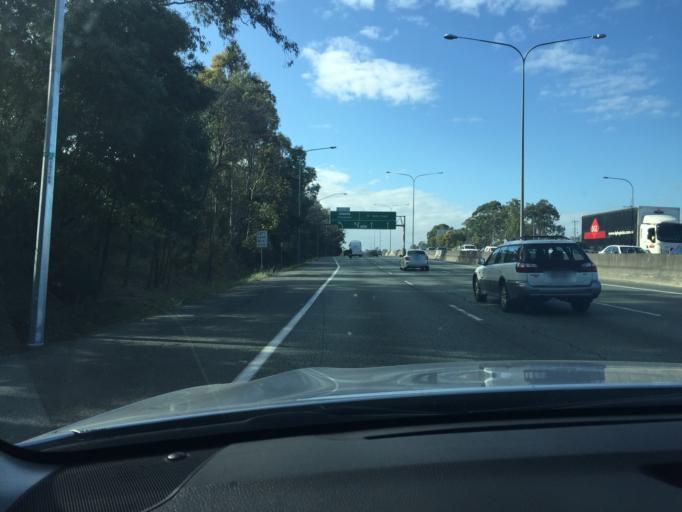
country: AU
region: Queensland
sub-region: Logan
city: Slacks Creek
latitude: -27.6525
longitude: 153.1611
